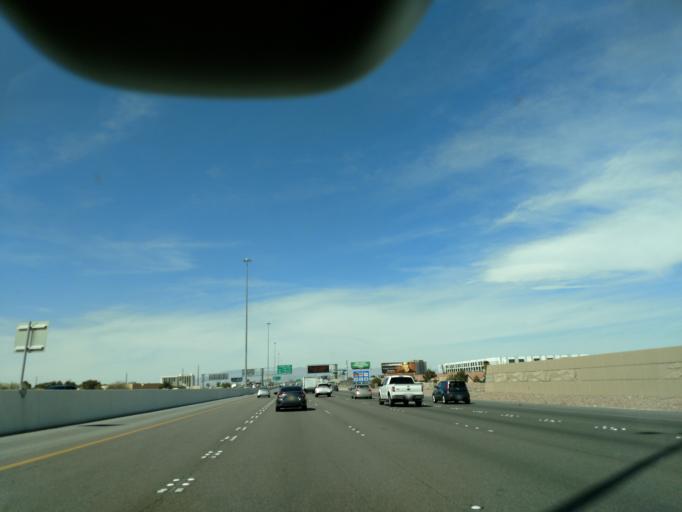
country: US
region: Nevada
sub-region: Clark County
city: Enterprise
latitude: 36.0226
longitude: -115.1805
